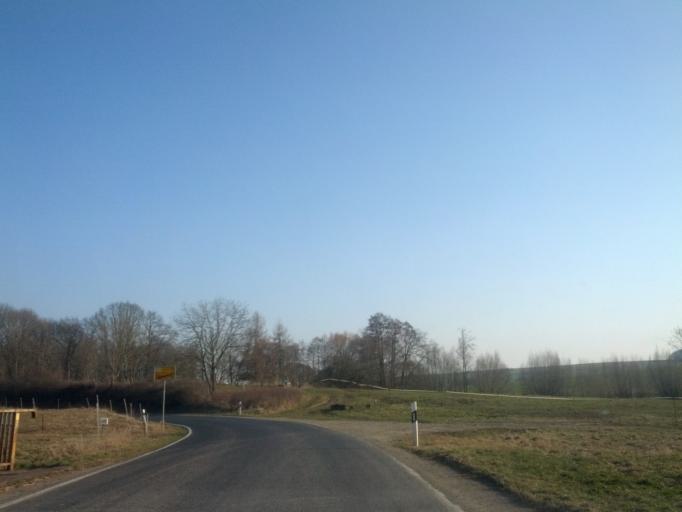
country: DE
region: Thuringia
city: Bischofroda
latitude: 51.0550
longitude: 10.3686
